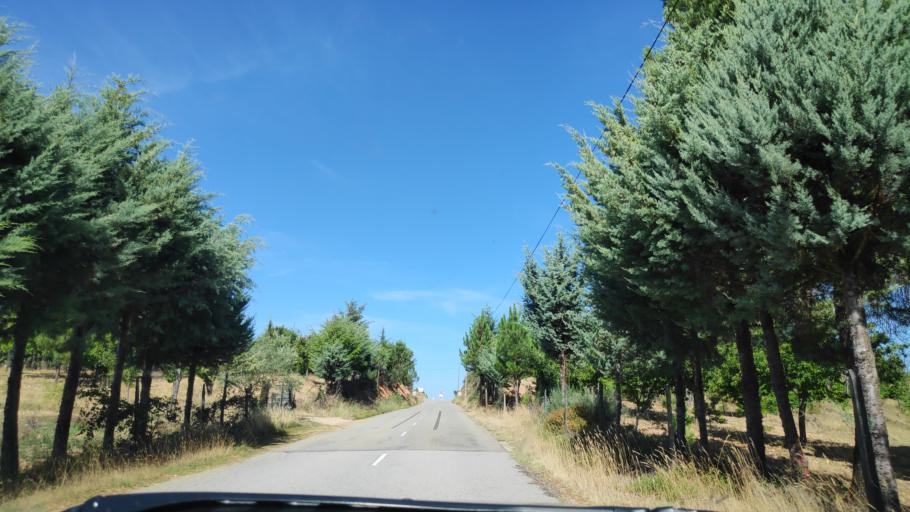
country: ES
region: Castille and Leon
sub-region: Provincia de Zamora
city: Alcanices
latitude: 41.6519
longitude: -6.3858
